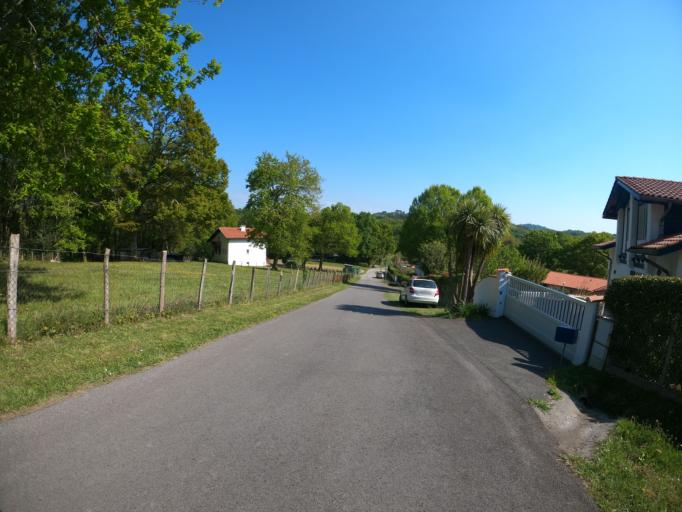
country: FR
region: Aquitaine
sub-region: Departement des Pyrenees-Atlantiques
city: Bassussarry
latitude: 43.4376
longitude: -1.5000
